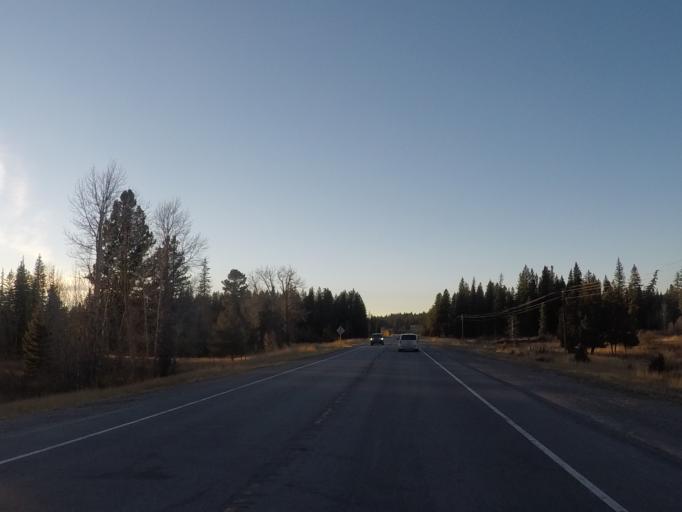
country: US
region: Montana
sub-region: Lewis and Clark County
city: Lincoln
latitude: 47.0009
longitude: -113.0374
